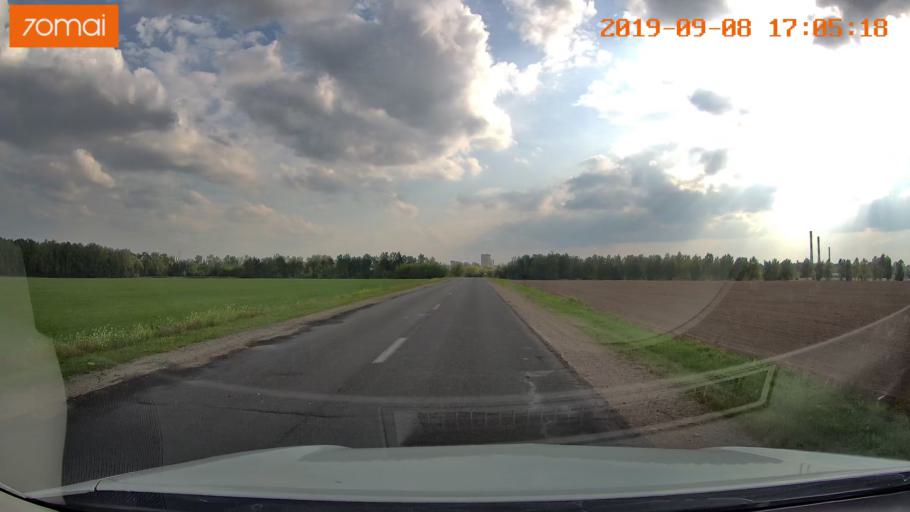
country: BY
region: Grodnenskaya
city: Hrodna
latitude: 53.6793
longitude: 23.9550
